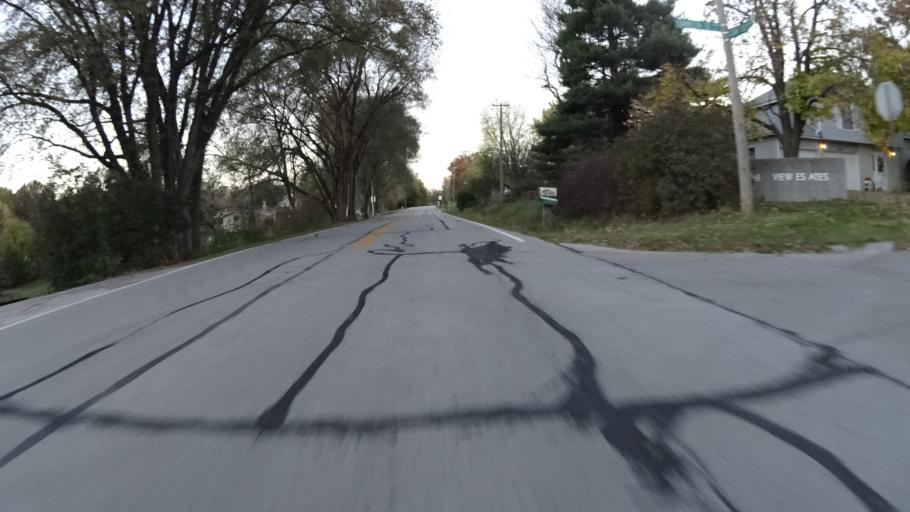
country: US
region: Nebraska
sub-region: Sarpy County
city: Offutt Air Force Base
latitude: 41.1785
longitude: -95.9528
